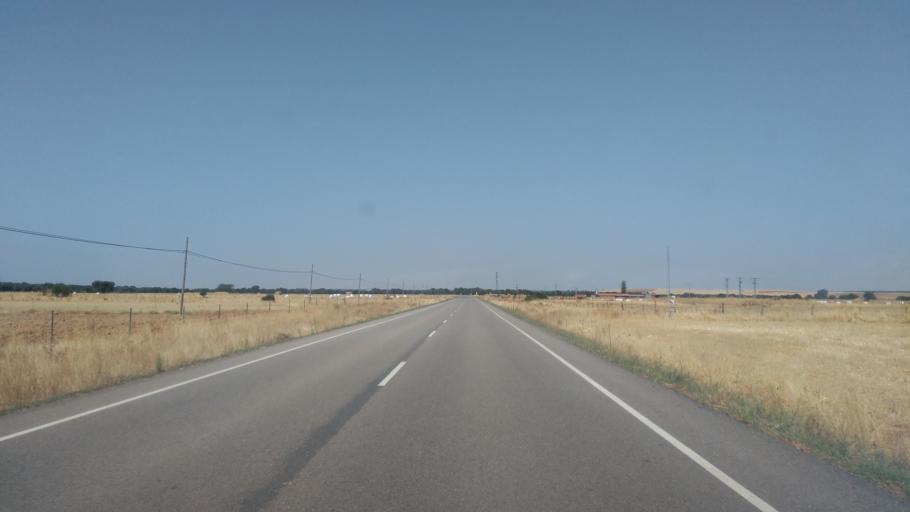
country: ES
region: Castille and Leon
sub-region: Provincia de Salamanca
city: Abusejo
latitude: 40.7166
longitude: -6.1468
